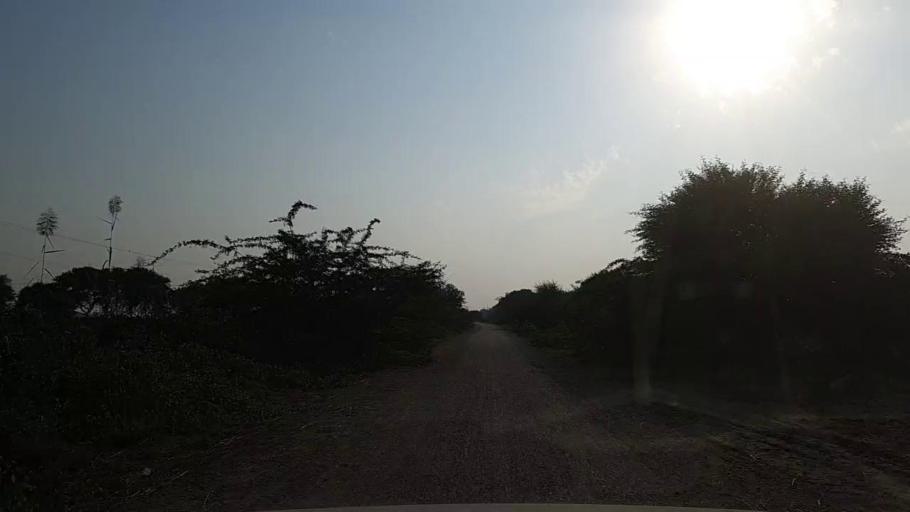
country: PK
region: Sindh
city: Mirpur Batoro
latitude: 24.7781
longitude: 68.2411
